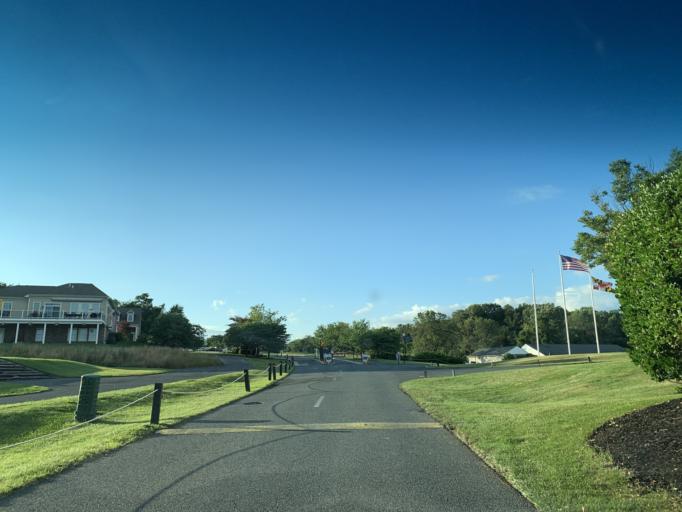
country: US
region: Maryland
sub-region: Harford County
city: Havre de Grace
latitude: 39.5424
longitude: -76.1330
